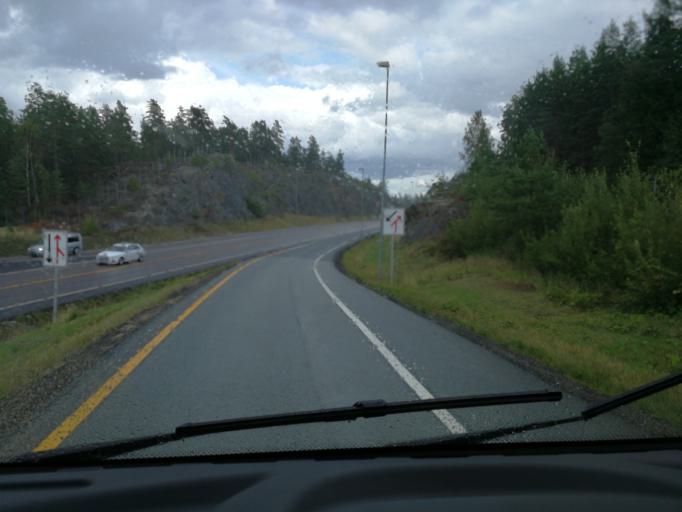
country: NO
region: Ostfold
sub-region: Marker
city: Orje
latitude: 59.5395
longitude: 11.5389
